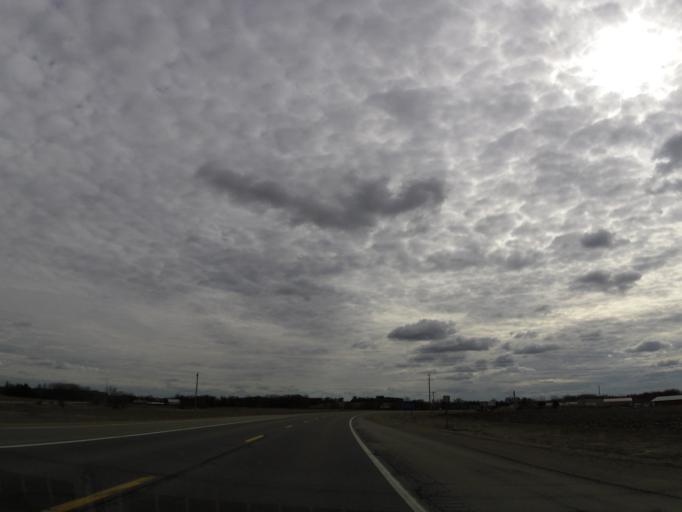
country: US
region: Iowa
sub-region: Chickasaw County
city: New Hampton
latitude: 43.0919
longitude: -92.2989
